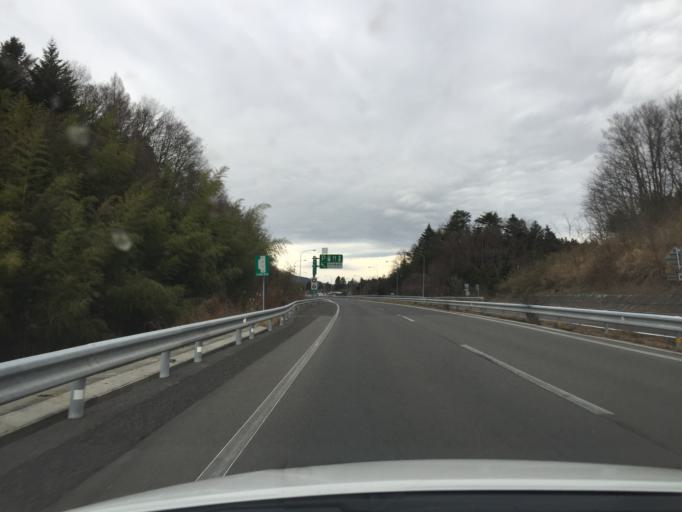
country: JP
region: Fukushima
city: Funehikimachi-funehiki
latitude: 37.3838
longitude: 140.5973
